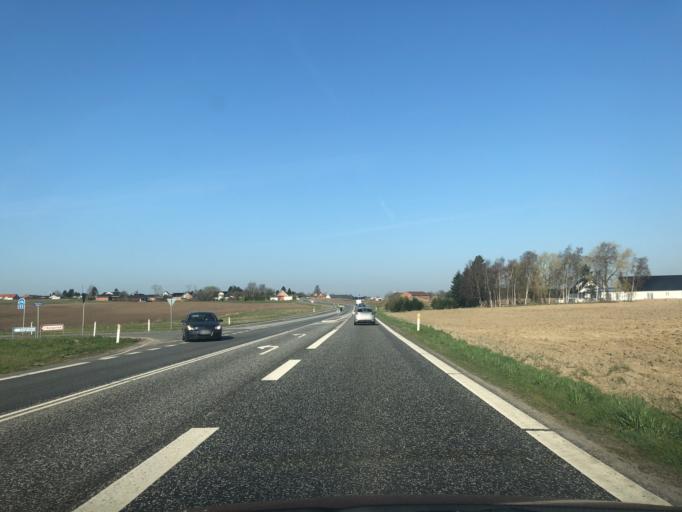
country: DK
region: Zealand
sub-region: Faxe Kommune
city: Ronnede
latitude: 55.2582
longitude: 12.0393
